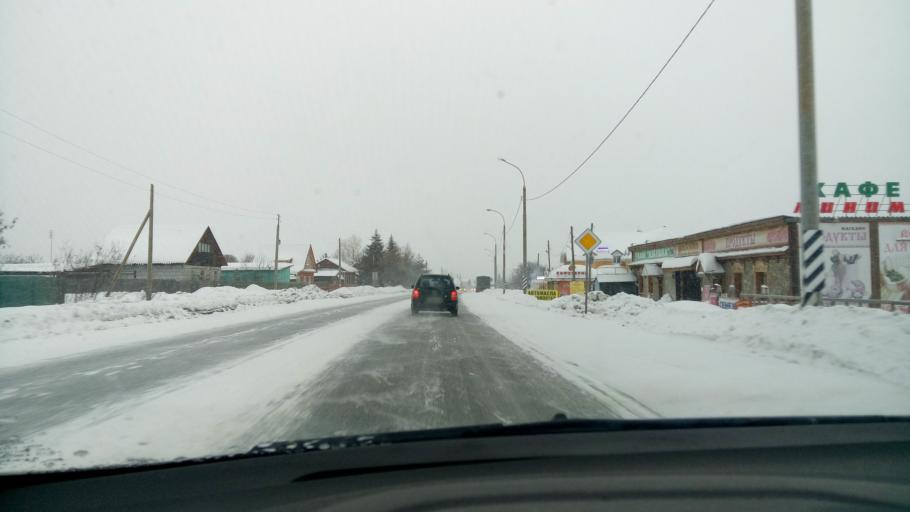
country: RU
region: Sverdlovsk
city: Verkhneye Dubrovo
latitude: 56.7365
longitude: 61.1123
